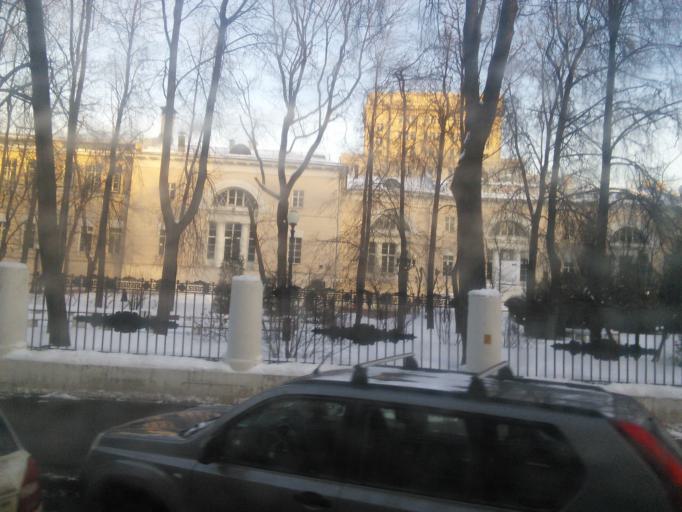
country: RU
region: Moscow
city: Lefortovo
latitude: 55.7664
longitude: 37.6835
